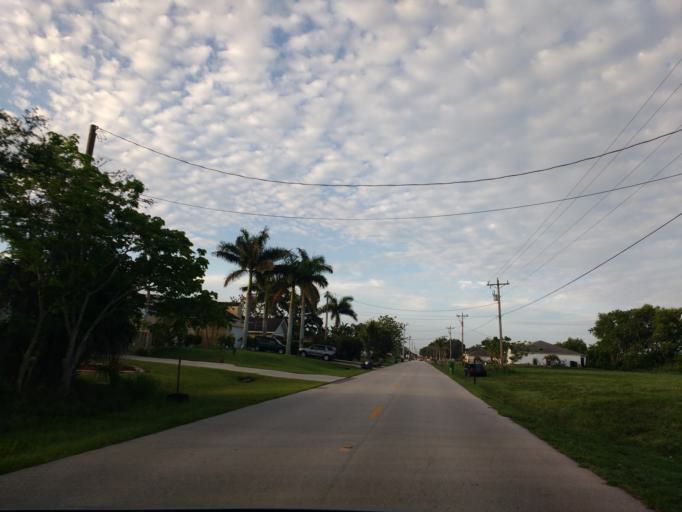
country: US
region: Florida
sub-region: Lee County
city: Cape Coral
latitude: 26.6257
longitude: -82.0153
